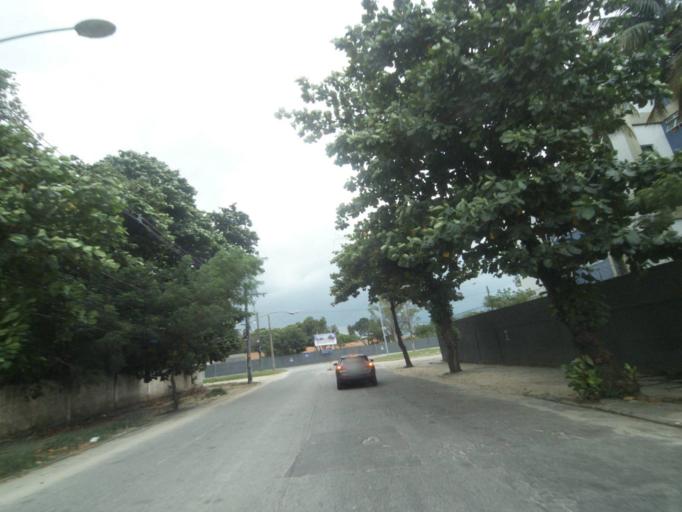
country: BR
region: Rio de Janeiro
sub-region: Nilopolis
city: Nilopolis
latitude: -22.8857
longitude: -43.3898
